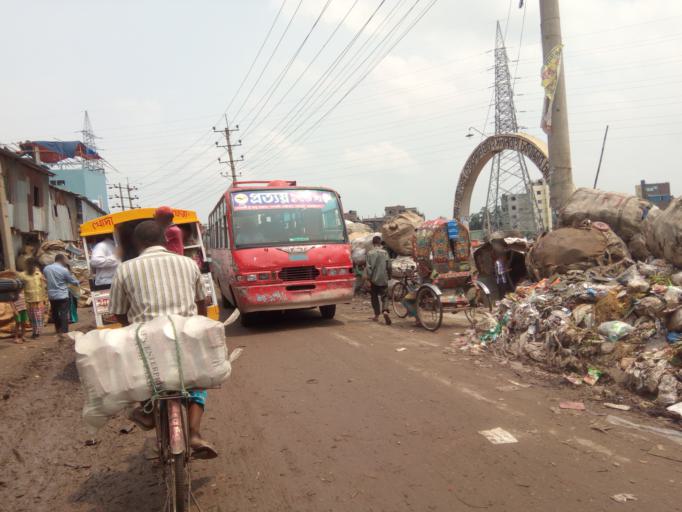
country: BD
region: Dhaka
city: Azimpur
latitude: 23.7125
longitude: 90.3874
